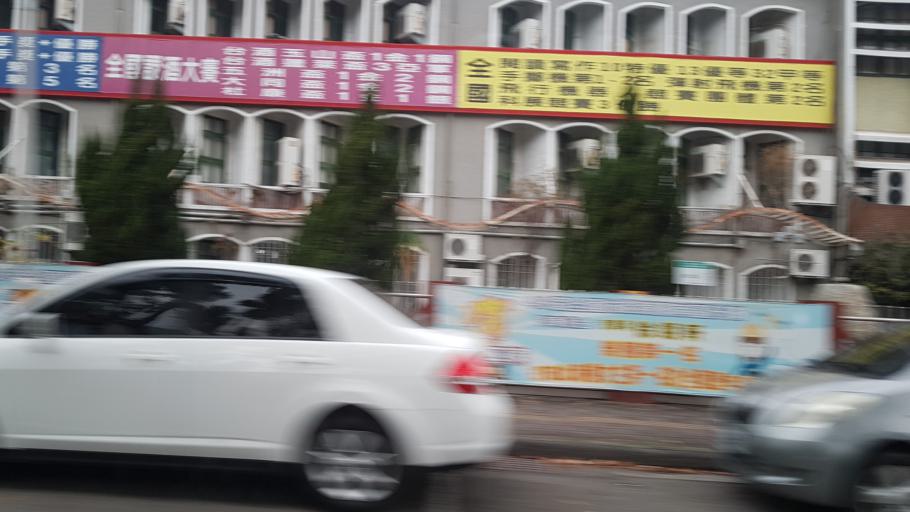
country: TW
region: Taiwan
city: Xinying
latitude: 23.3165
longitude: 120.3121
